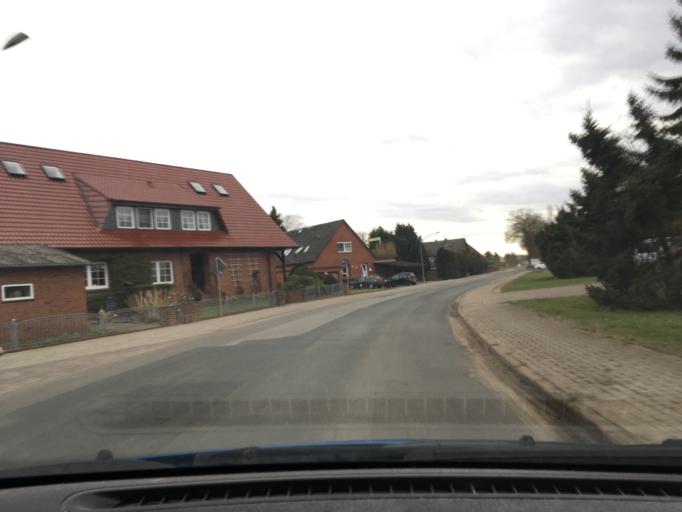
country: DE
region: Lower Saxony
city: Handorf
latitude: 53.3635
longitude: 10.3372
